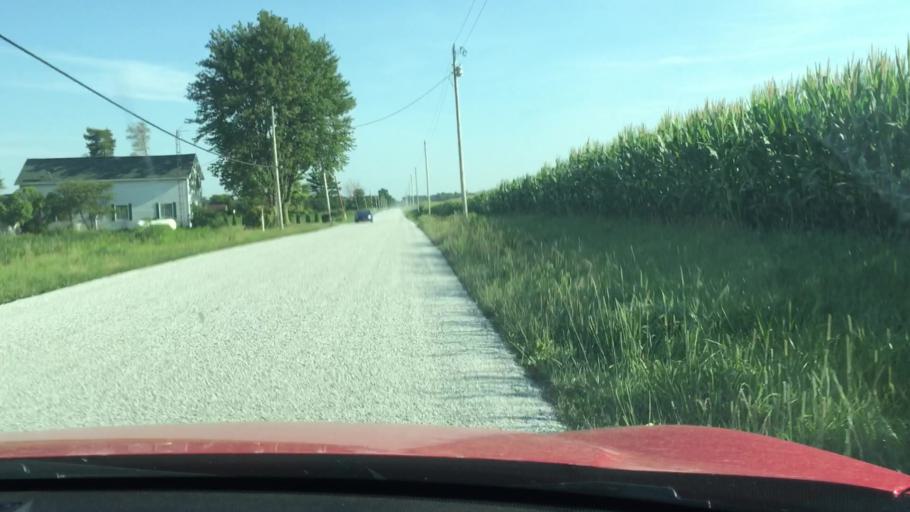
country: US
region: Ohio
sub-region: Hardin County
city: Ada
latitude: 40.7540
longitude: -83.8424
